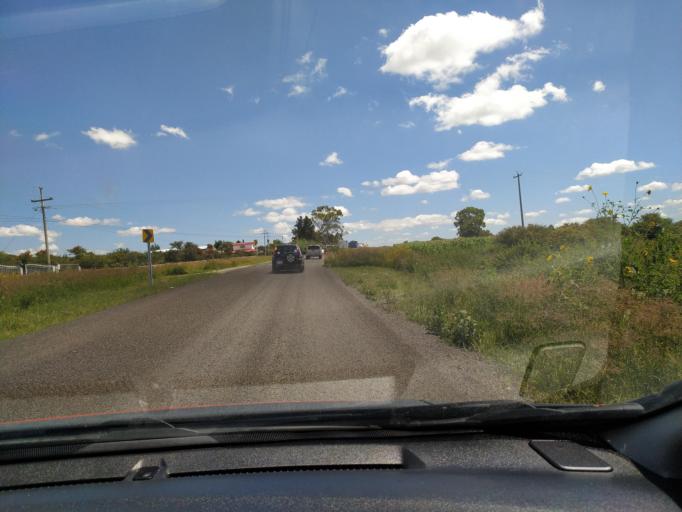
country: MX
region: Jalisco
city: San Diego de Alejandria
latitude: 21.0042
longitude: -102.0836
